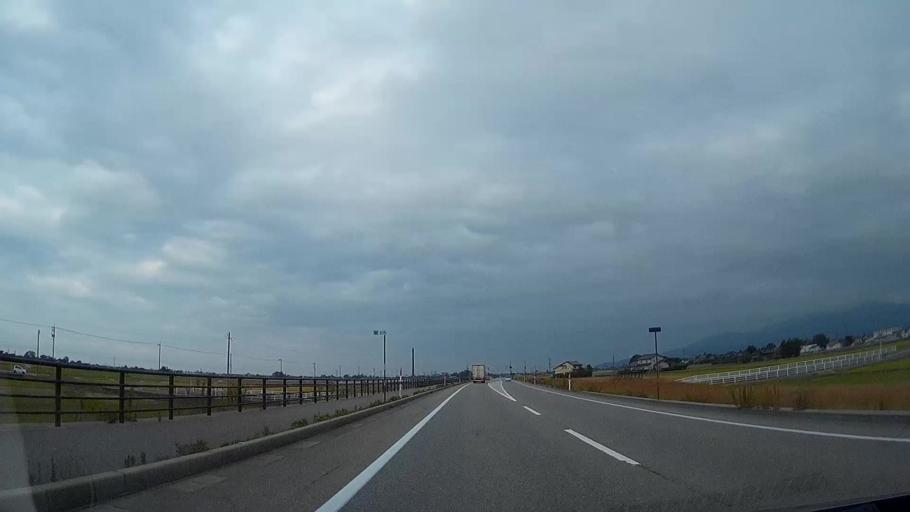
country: JP
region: Toyama
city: Nyuzen
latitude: 36.9254
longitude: 137.4720
